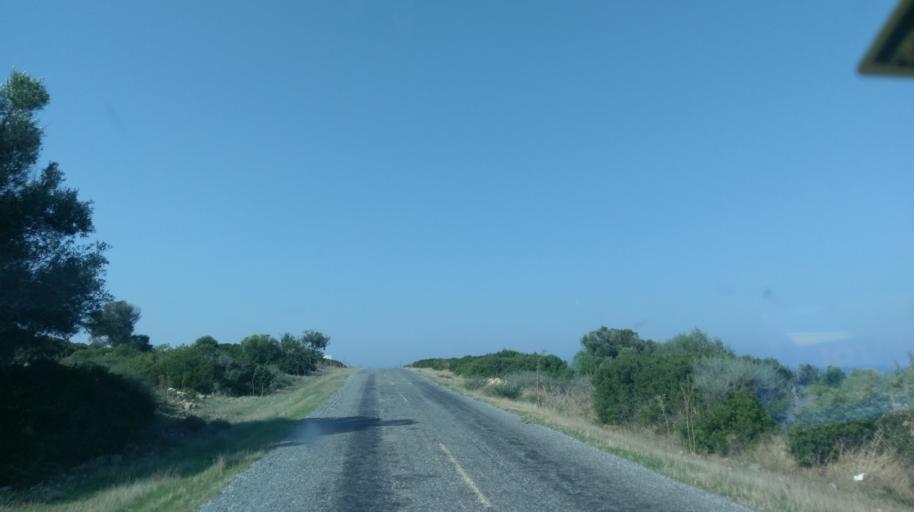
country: CY
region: Lefkosia
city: Morfou
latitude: 35.3788
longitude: 32.9682
